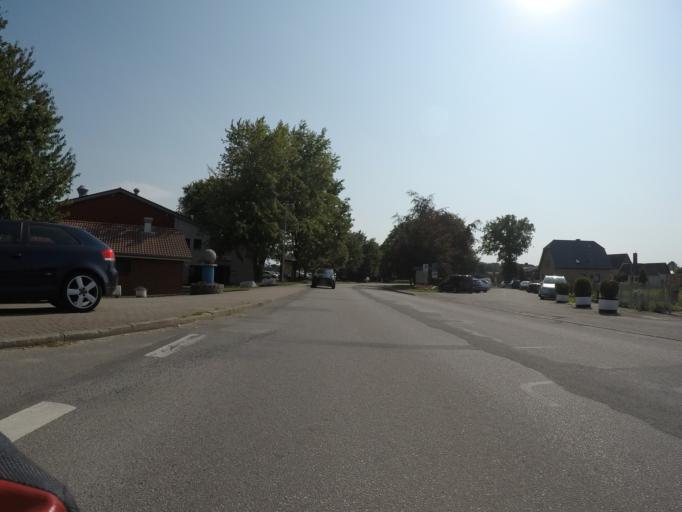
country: DE
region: Schleswig-Holstein
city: Todesfelde
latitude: 53.8993
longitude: 10.1835
